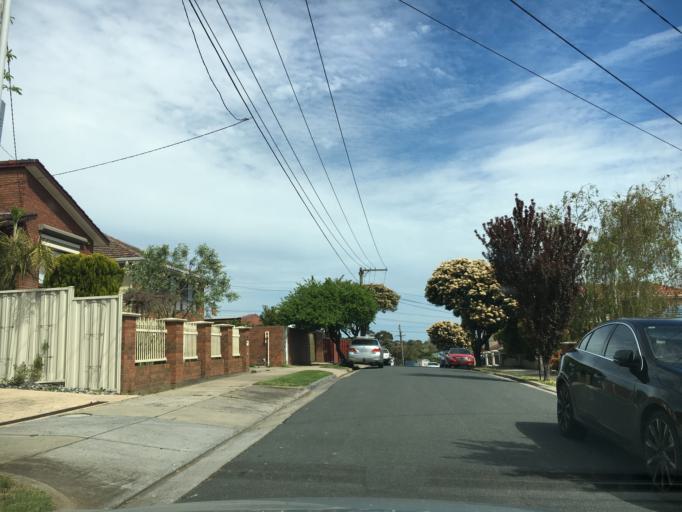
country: AU
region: Victoria
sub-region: Monash
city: Chadstone
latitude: -37.8956
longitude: 145.1022
